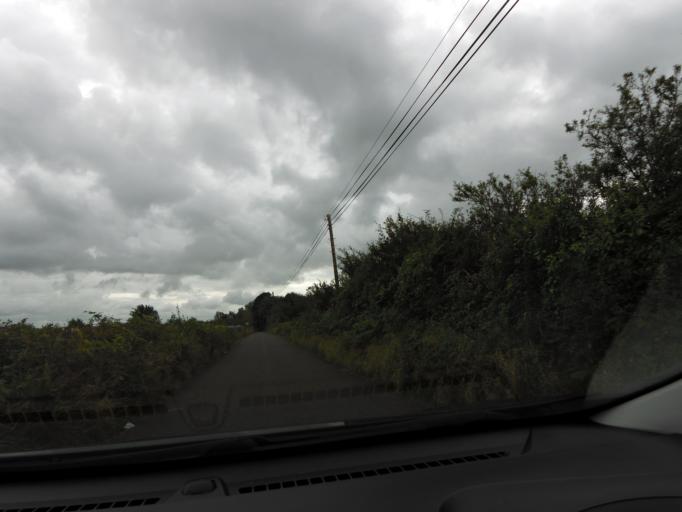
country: IE
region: Connaught
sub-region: County Galway
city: Athenry
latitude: 53.3282
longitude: -8.7870
